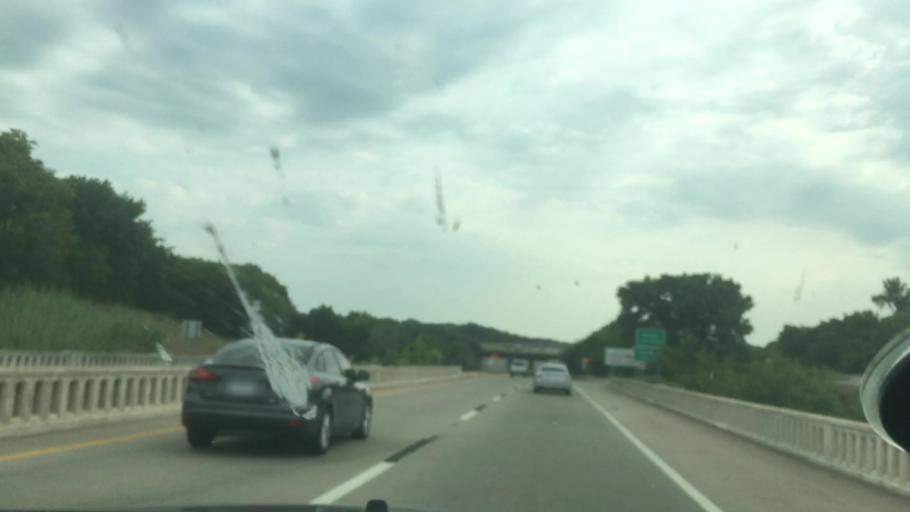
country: US
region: Oklahoma
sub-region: Bryan County
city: Colbert
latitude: 33.8244
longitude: -96.5314
